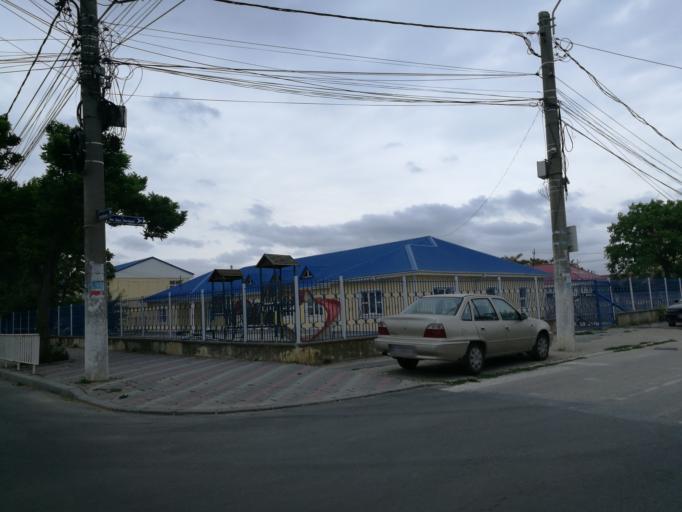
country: RO
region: Constanta
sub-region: Municipiul Mangalia
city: Mangalia
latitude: 43.8185
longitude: 28.5743
